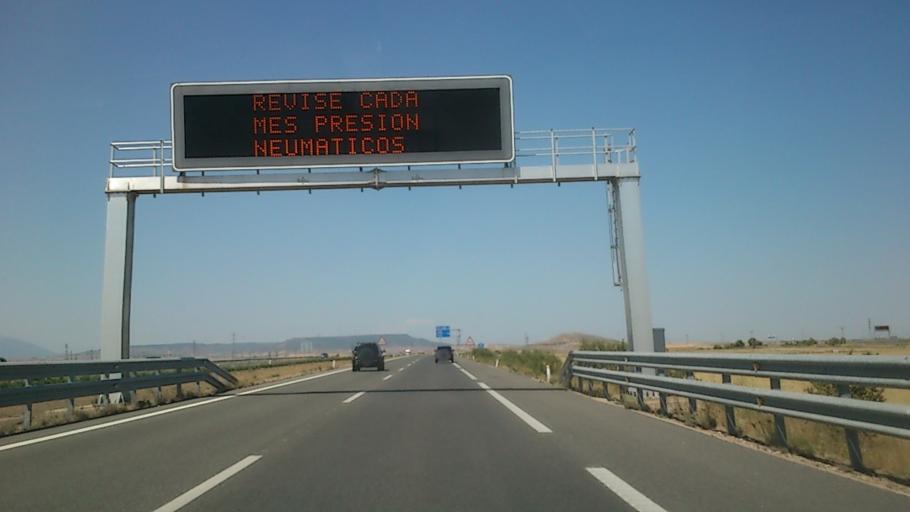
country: ES
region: Aragon
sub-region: Provincia de Zaragoza
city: Gallur
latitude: 41.8463
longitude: -1.3609
